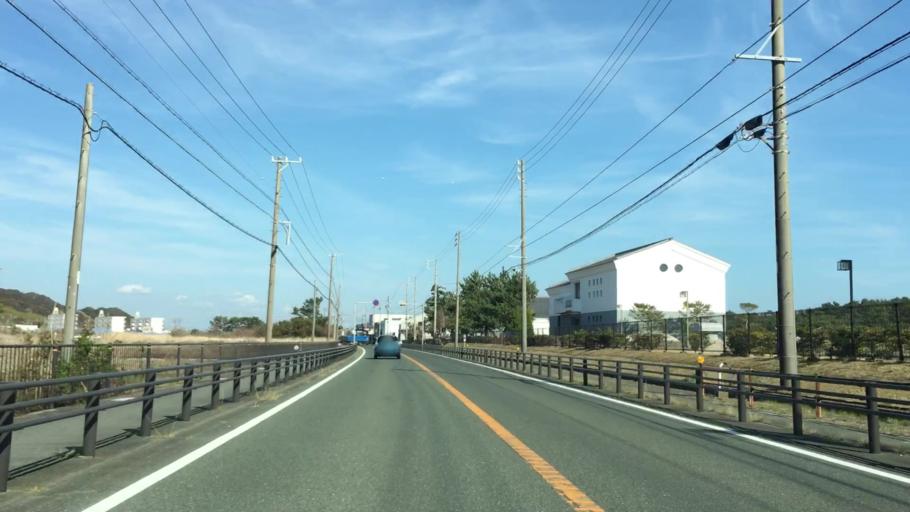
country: JP
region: Shizuoka
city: Kosai-shi
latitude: 34.6813
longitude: 137.5380
